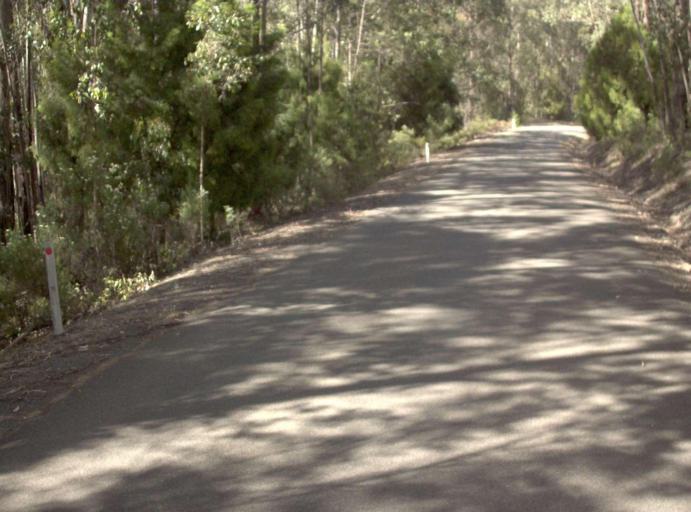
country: AU
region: Victoria
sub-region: East Gippsland
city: Lakes Entrance
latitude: -37.4242
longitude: 148.1279
